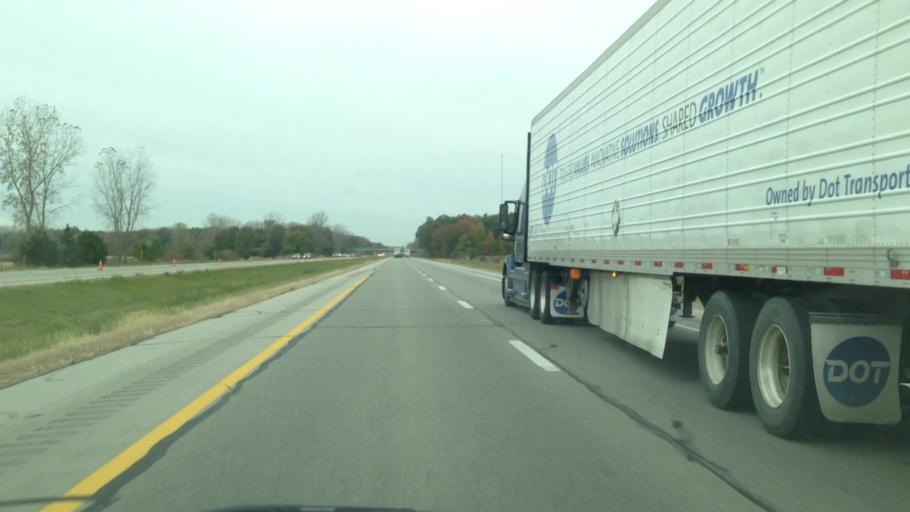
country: US
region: Ohio
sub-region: Lucas County
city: Holland
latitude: 41.5918
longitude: -83.7505
